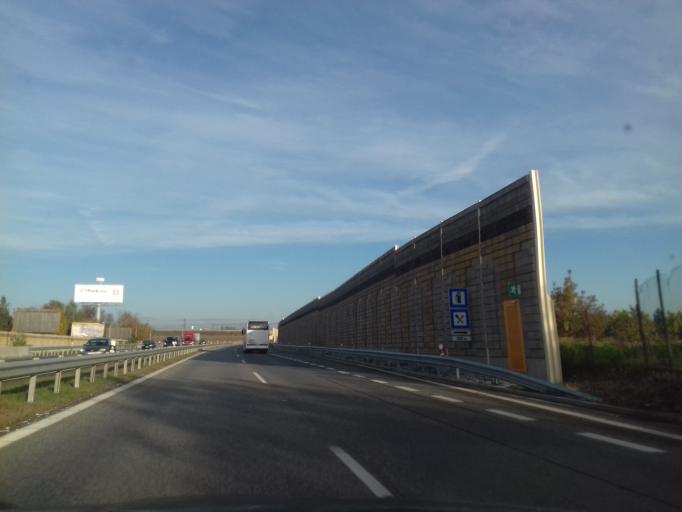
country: SK
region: Trnavsky
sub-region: Okres Trnava
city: Trnava
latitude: 48.3100
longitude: 17.6487
